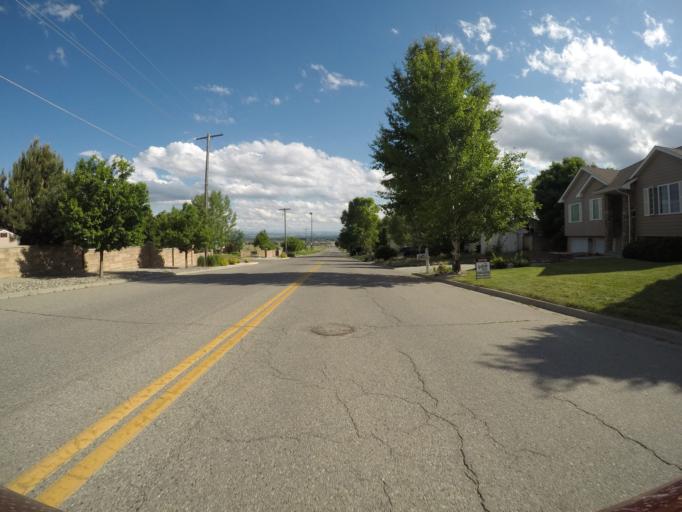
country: US
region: Montana
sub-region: Yellowstone County
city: Billings
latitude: 45.8046
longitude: -108.6527
